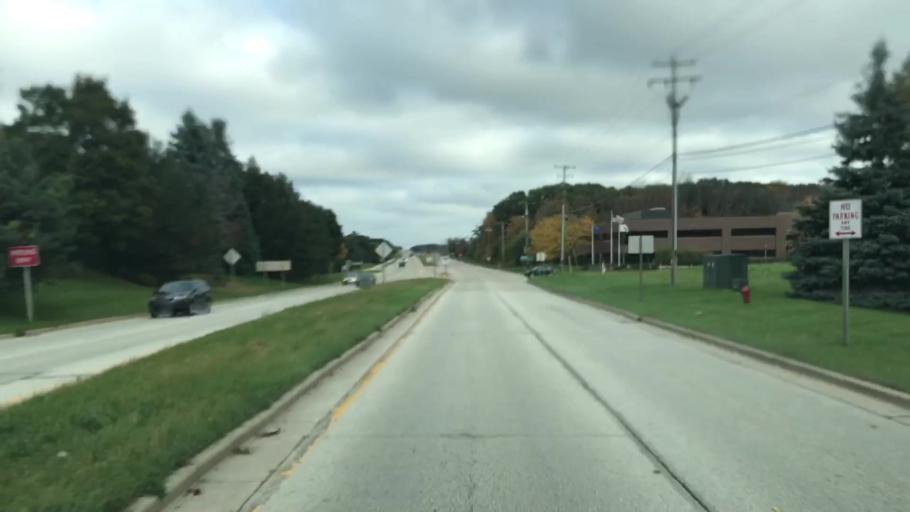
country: US
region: Wisconsin
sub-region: Waukesha County
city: Waukesha
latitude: 43.0546
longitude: -88.2255
